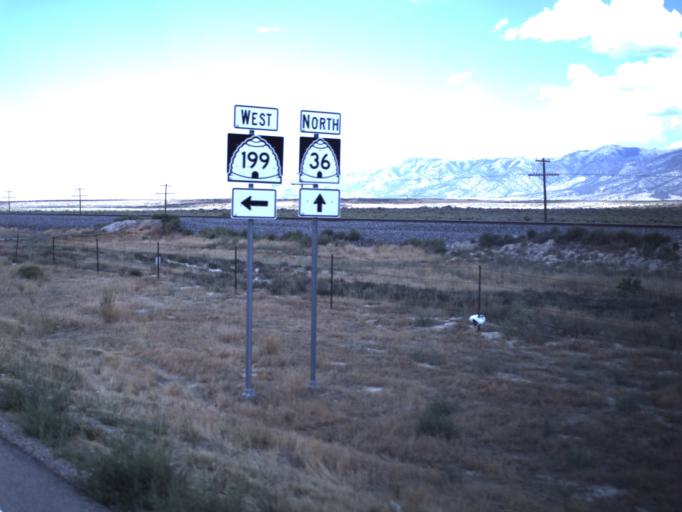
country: US
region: Utah
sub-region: Tooele County
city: Tooele
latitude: 40.3365
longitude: -112.4094
